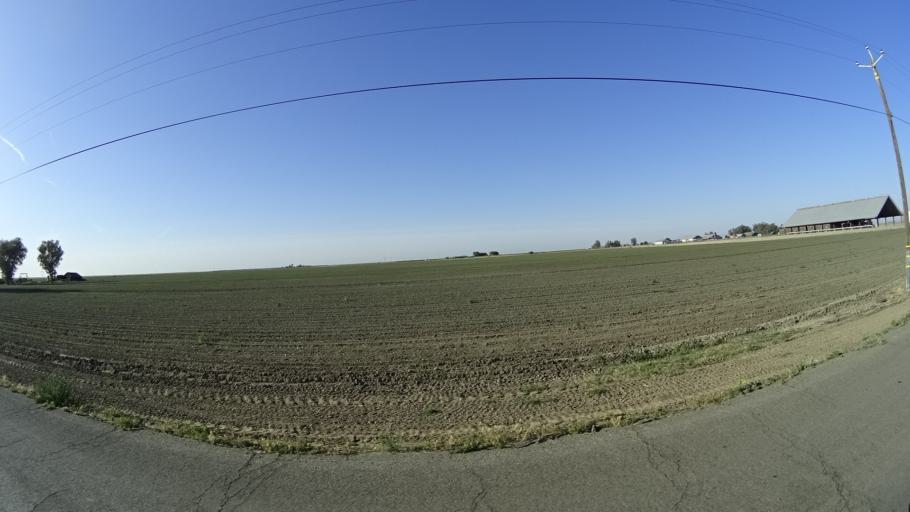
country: US
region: California
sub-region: Kings County
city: Stratford
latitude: 36.1674
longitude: -119.8079
